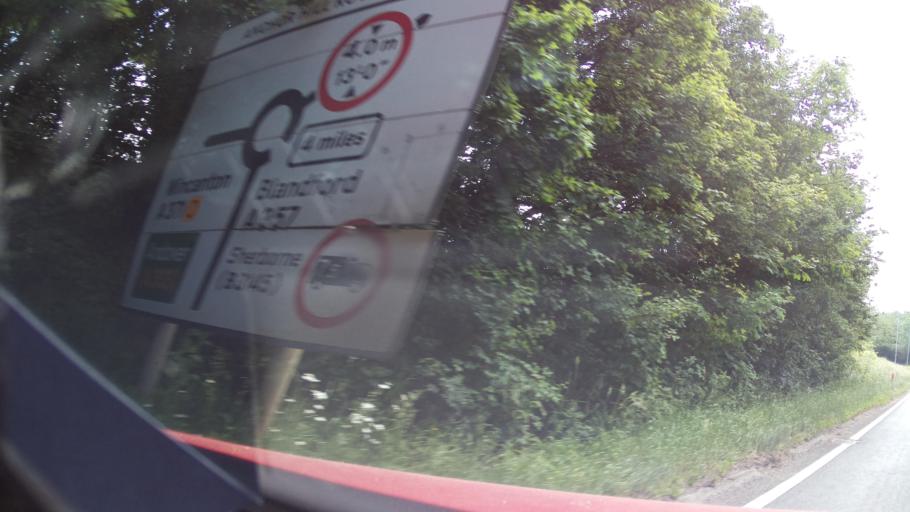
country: GB
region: England
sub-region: Somerset
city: Wincanton
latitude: 51.0484
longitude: -2.4361
